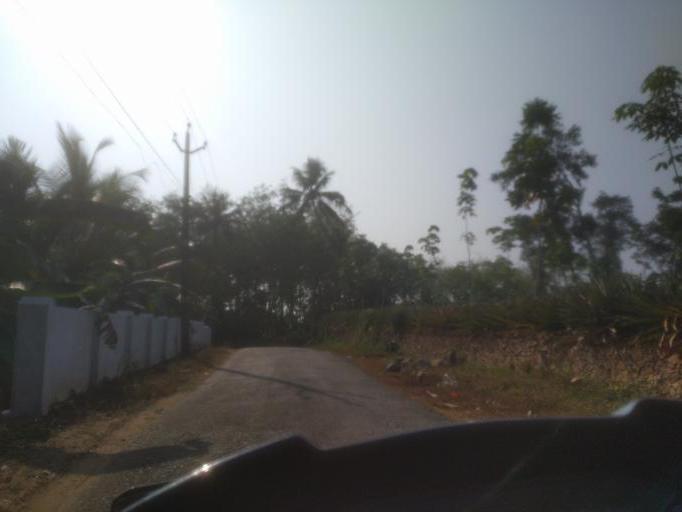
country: IN
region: Kerala
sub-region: Ernakulam
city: Piravam
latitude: 9.8502
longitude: 76.5305
